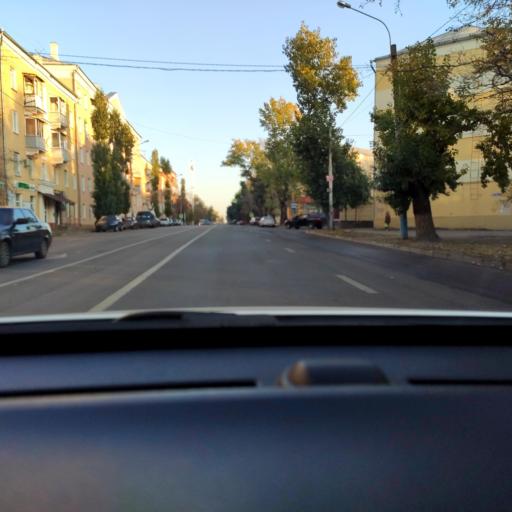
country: RU
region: Voronezj
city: Maslovka
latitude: 51.6216
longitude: 39.2420
